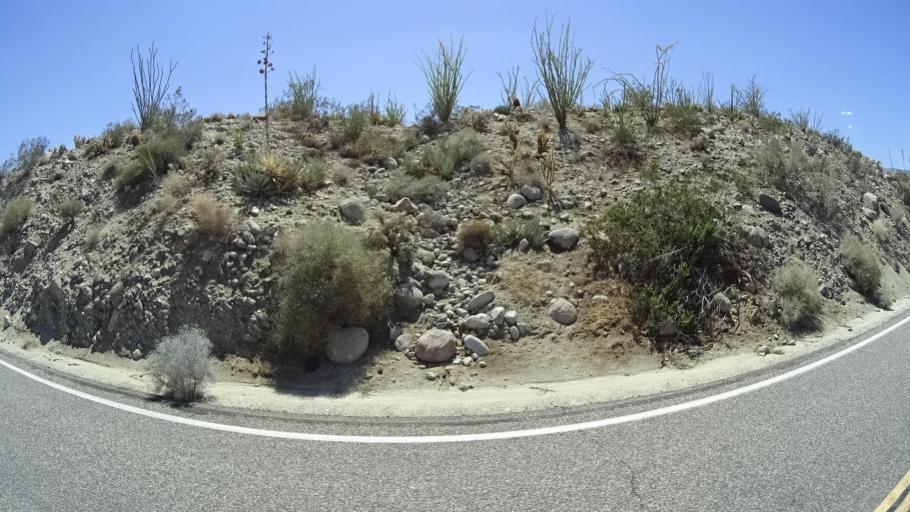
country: US
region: California
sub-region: San Diego County
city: Borrego Springs
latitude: 33.1333
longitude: -116.3138
